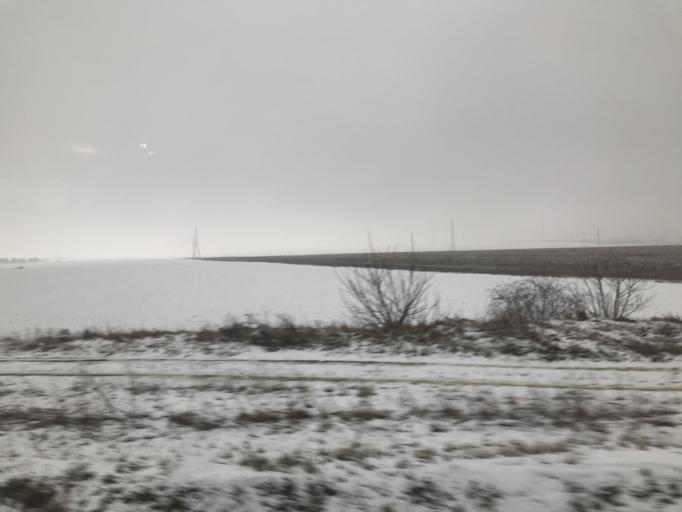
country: HU
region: Gyor-Moson-Sopron
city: Toltestava
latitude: 47.6875
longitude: 17.7379
